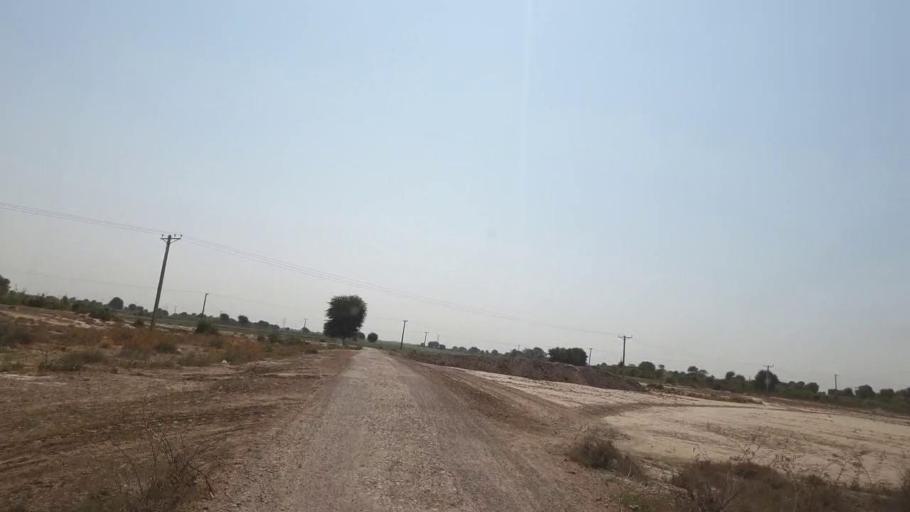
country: PK
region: Sindh
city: Kunri
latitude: 25.0921
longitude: 69.5280
